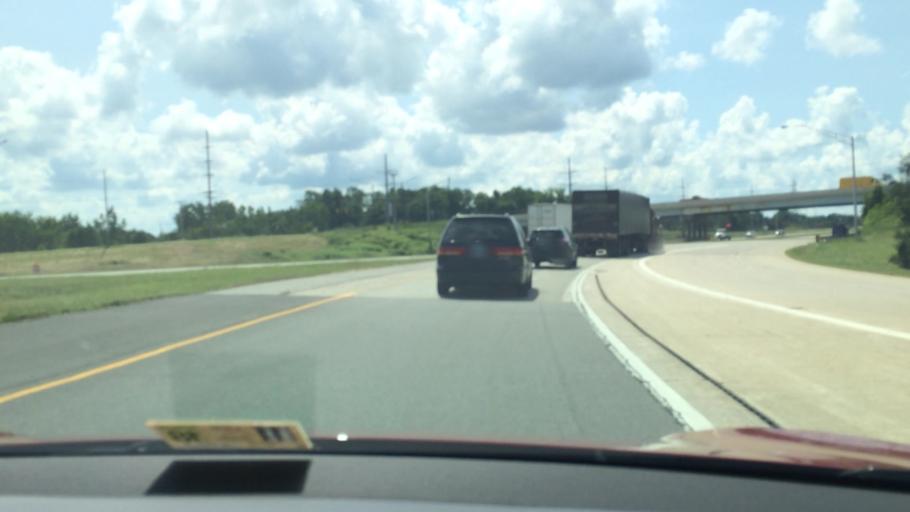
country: US
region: Indiana
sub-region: Saint Joseph County
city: South Bend
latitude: 41.7241
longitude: -86.3399
